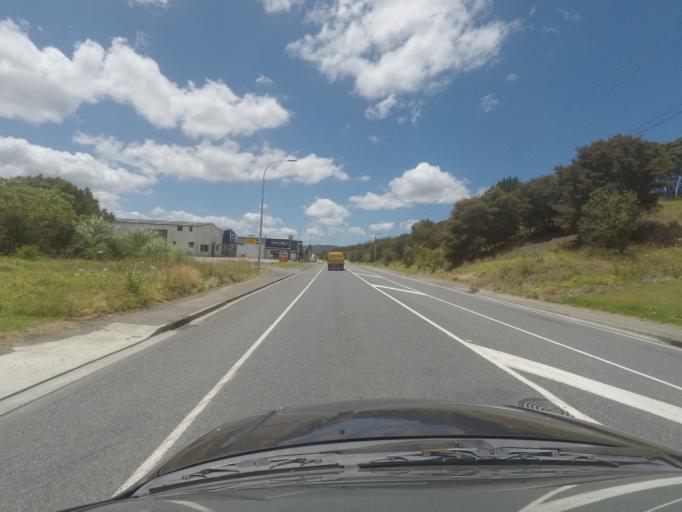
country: NZ
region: Northland
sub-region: Whangarei
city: Whangarei
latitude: -35.7435
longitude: 174.3287
